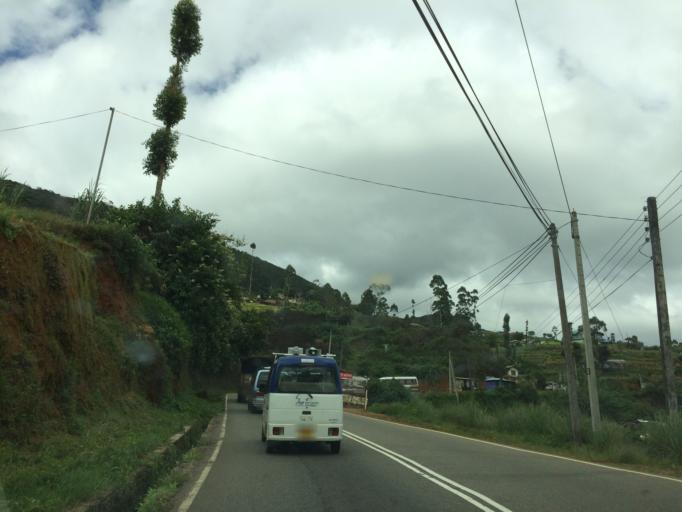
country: LK
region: Central
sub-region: Nuwara Eliya District
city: Nuwara Eliya
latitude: 7.0176
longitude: 80.7277
